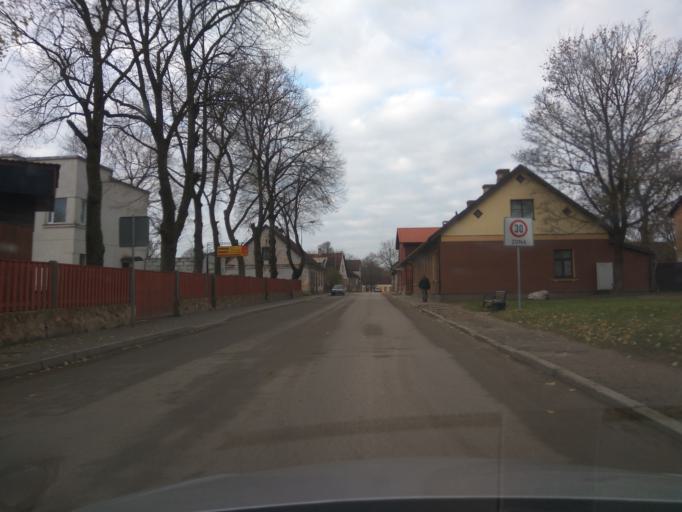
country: LV
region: Kuldigas Rajons
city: Kuldiga
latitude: 56.9645
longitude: 21.9760
